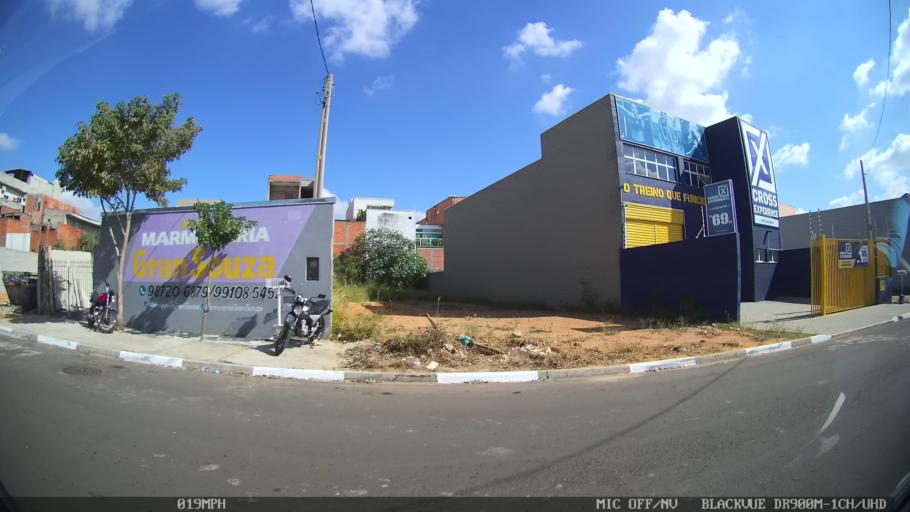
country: BR
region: Sao Paulo
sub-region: Hortolandia
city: Hortolandia
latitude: -22.8840
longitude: -47.2148
